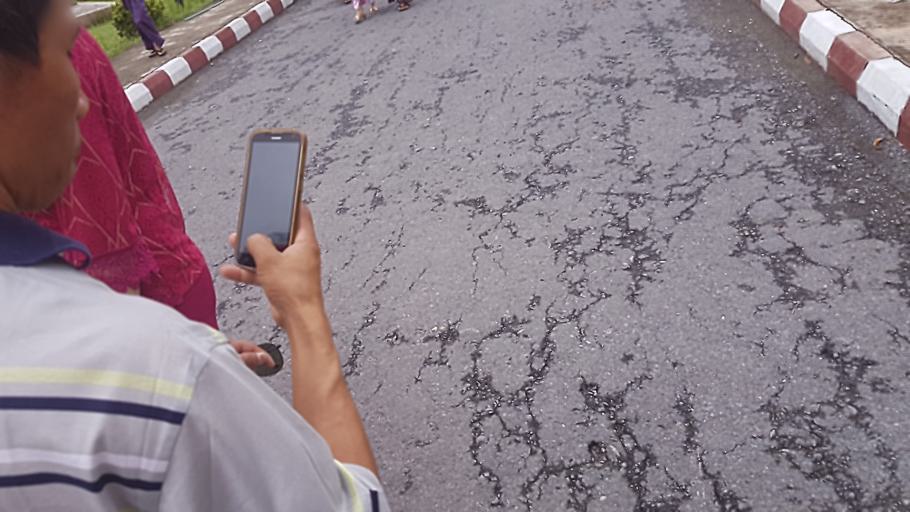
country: MM
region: Mandalay
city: Mandalay
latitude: 21.9548
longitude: 96.0893
